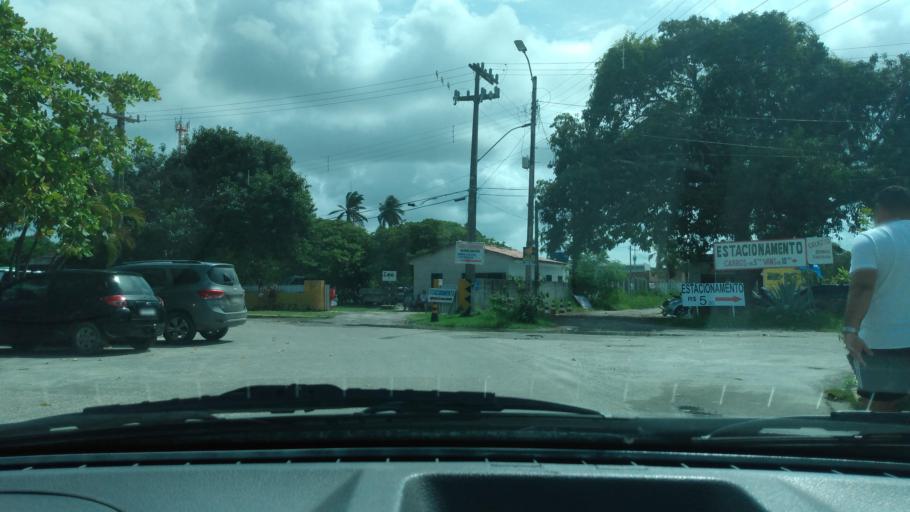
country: BR
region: Pernambuco
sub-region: Cabo De Santo Agostinho
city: Cabo
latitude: -8.3554
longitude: -34.9564
